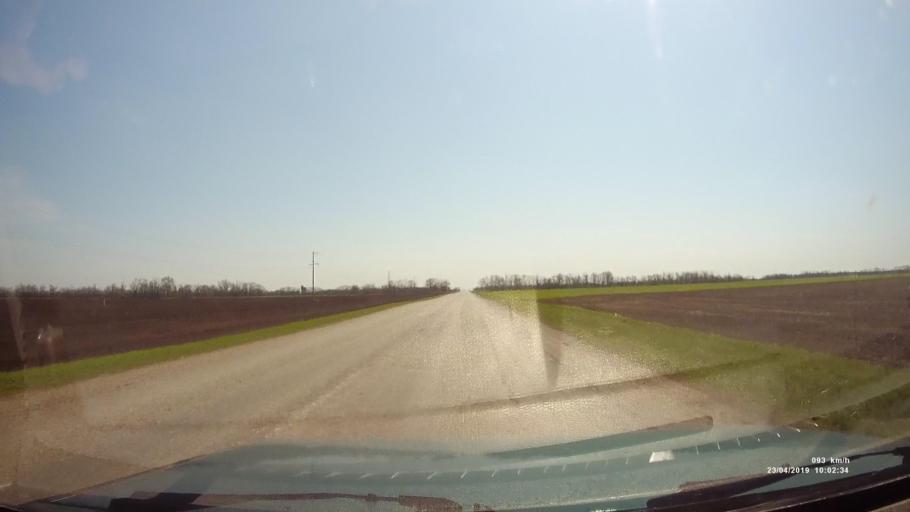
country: RU
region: Rostov
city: Sovetskoye
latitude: 46.7592
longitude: 42.1728
